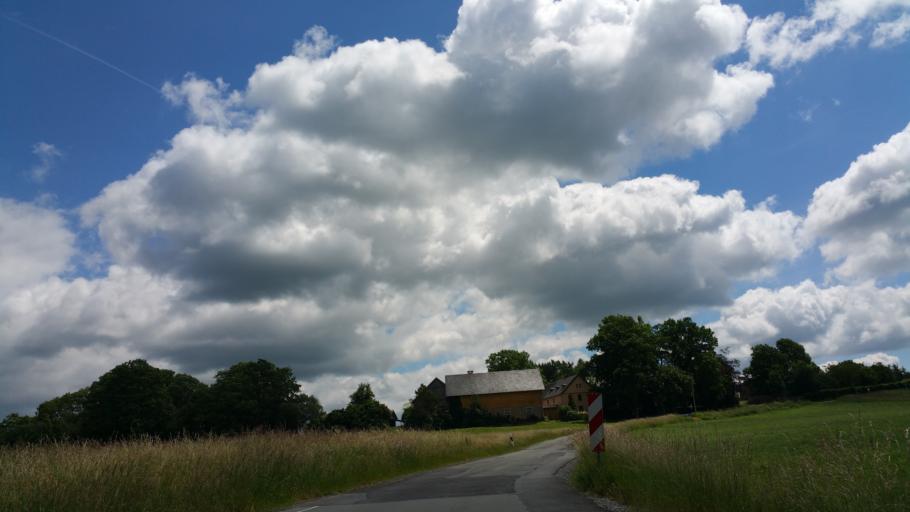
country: DE
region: Bavaria
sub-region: Upper Franconia
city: Schwarzenbach an der Saale
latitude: 50.1944
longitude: 11.9240
